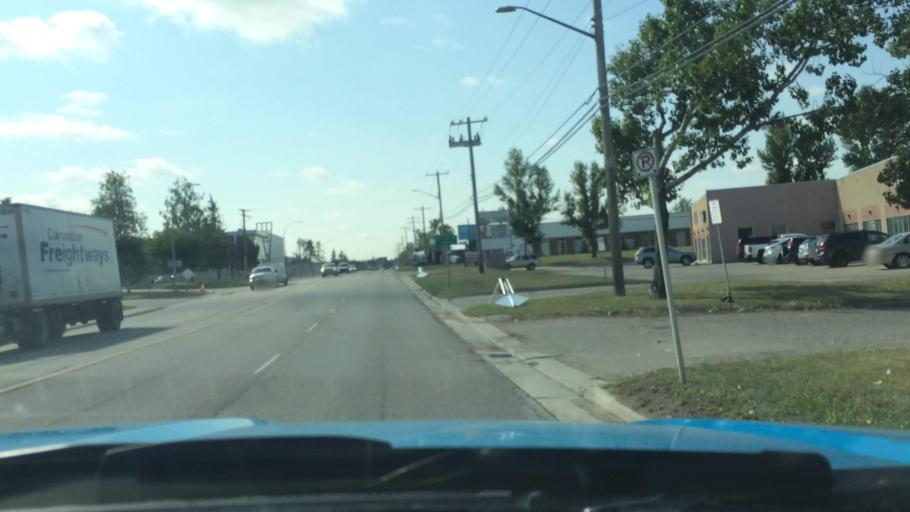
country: CA
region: Alberta
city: Calgary
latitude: 51.0882
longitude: -114.0317
